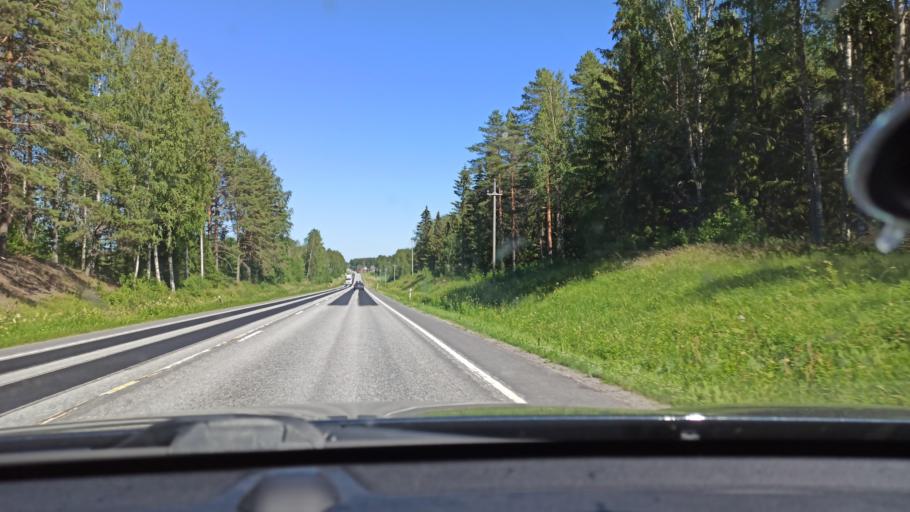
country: FI
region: Ostrobothnia
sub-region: Vaasa
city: Voera
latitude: 63.2065
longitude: 22.1496
